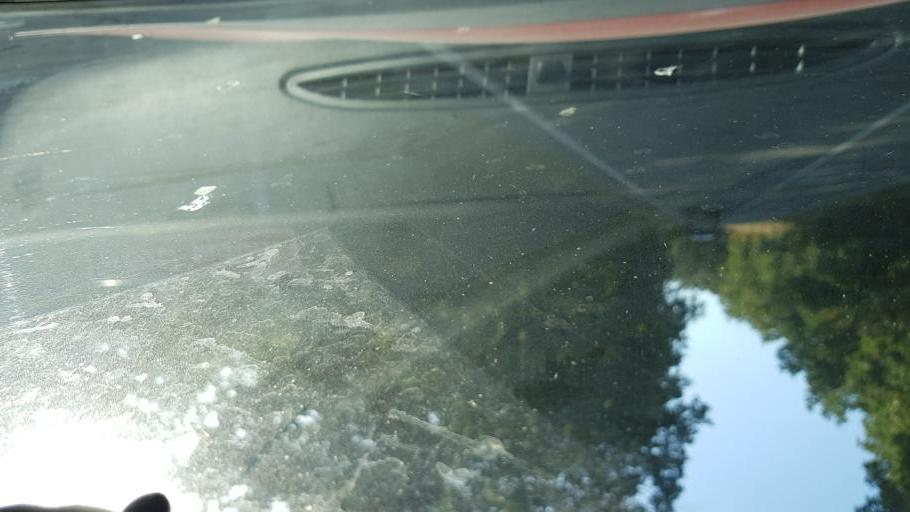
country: ES
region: Castille and Leon
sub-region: Provincia de Segovia
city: San Ildefonso
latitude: 40.8729
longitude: -4.0214
